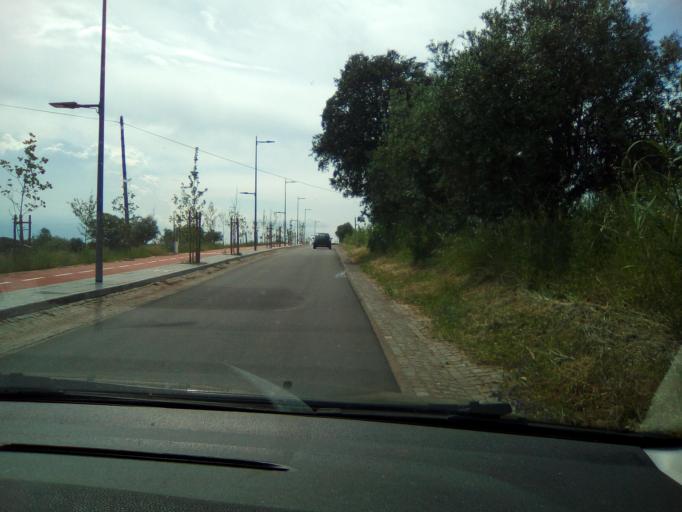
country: PT
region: Portalegre
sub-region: Avis
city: Avis
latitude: 39.0547
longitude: -7.9054
